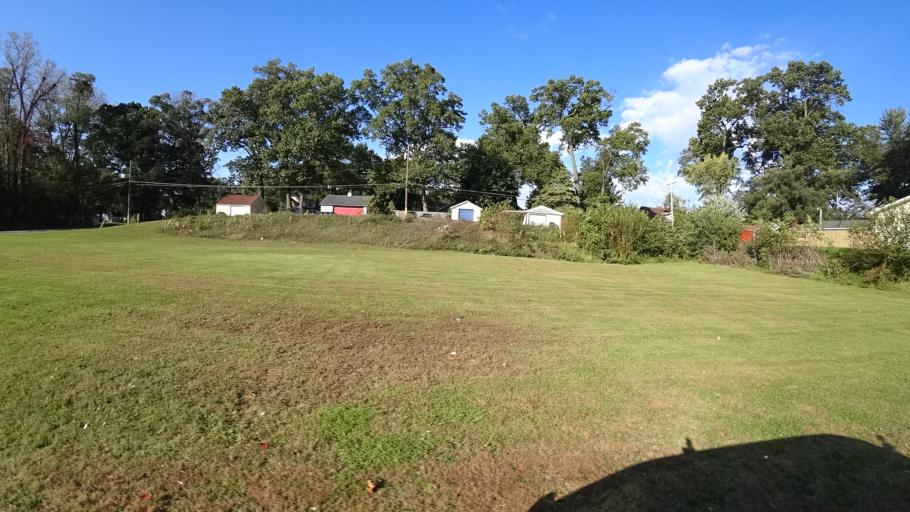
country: US
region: Indiana
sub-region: LaPorte County
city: Trail Creek
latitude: 41.7063
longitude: -86.8746
